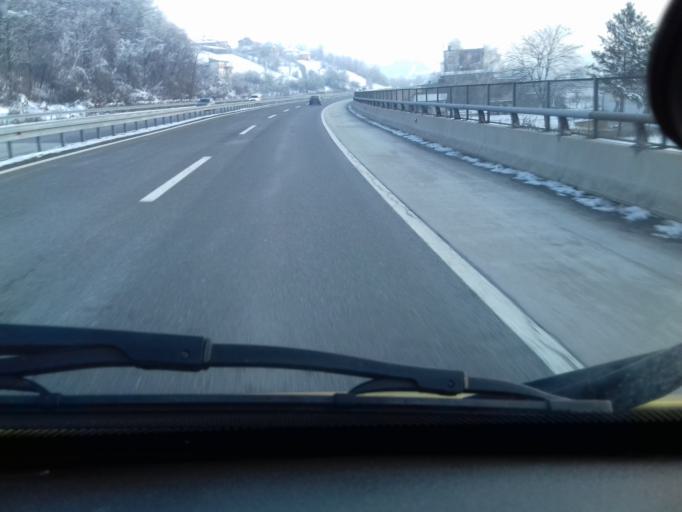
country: BA
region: Federation of Bosnia and Herzegovina
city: Visoko
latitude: 44.0031
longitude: 18.1776
